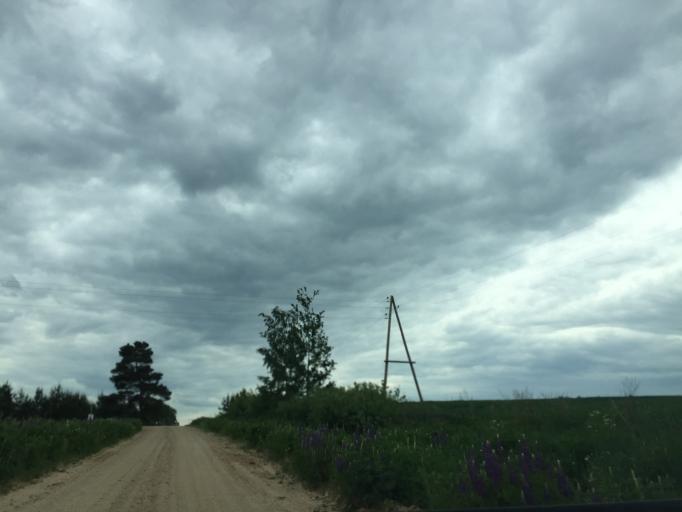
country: LV
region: Aglona
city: Aglona
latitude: 56.1672
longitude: 27.2530
